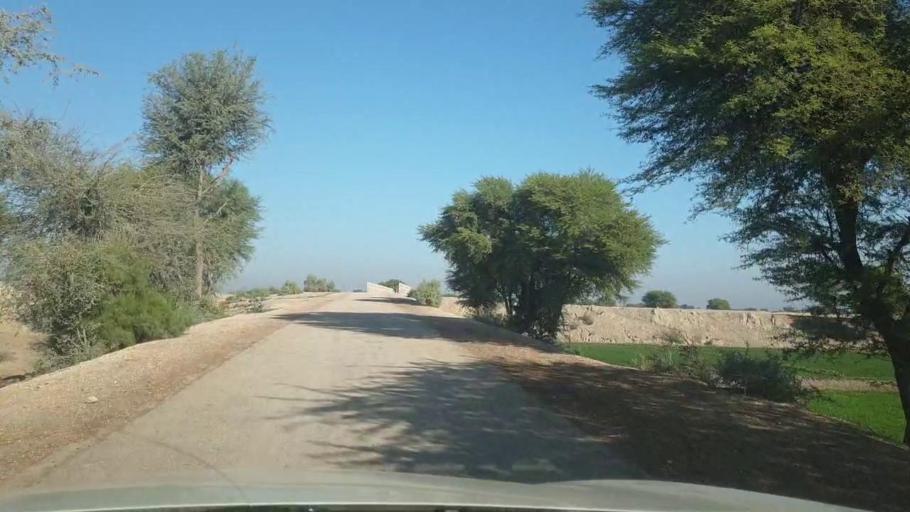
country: PK
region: Sindh
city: Bhan
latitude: 26.5576
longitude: 67.6640
